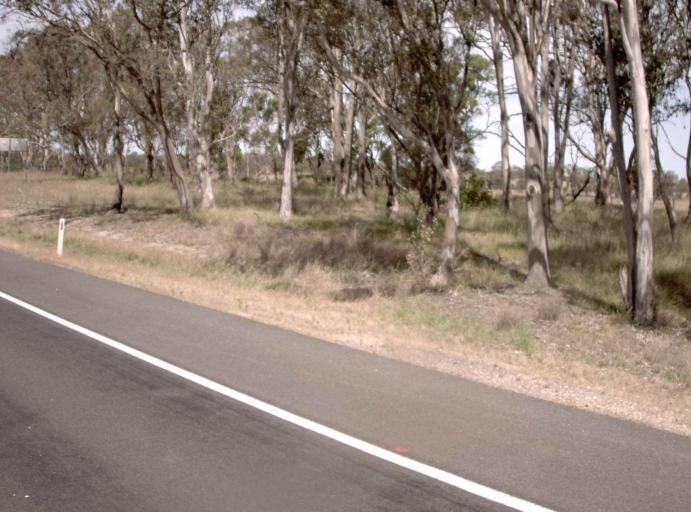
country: AU
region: Victoria
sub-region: East Gippsland
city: Bairnsdale
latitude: -37.8985
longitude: 147.3620
